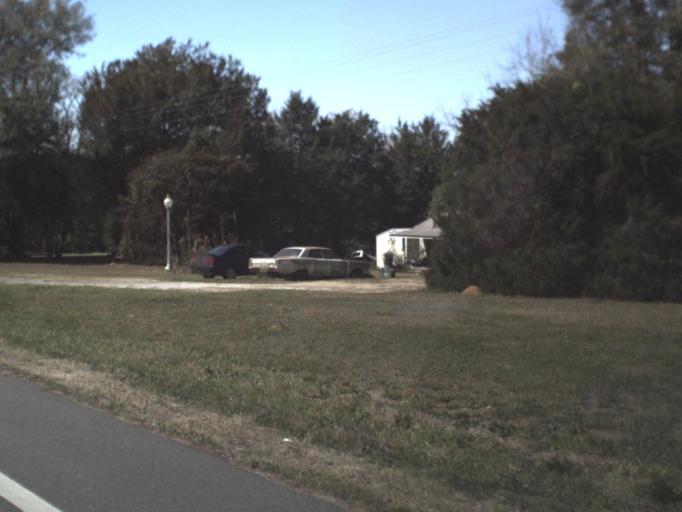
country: US
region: Florida
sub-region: Gadsden County
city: Chattahoochee
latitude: 30.7025
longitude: -84.7874
